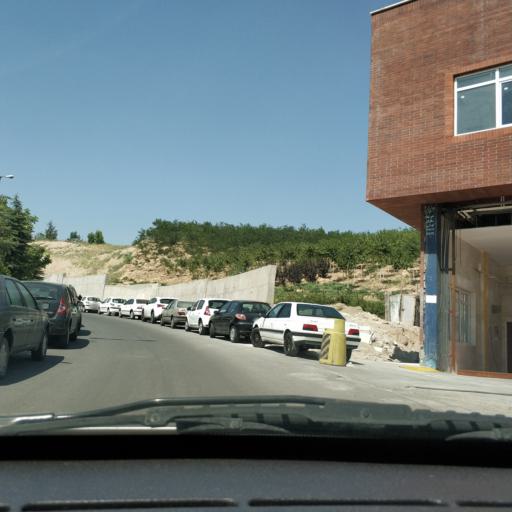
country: IR
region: Tehran
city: Tajrish
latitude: 35.7500
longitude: 51.4354
